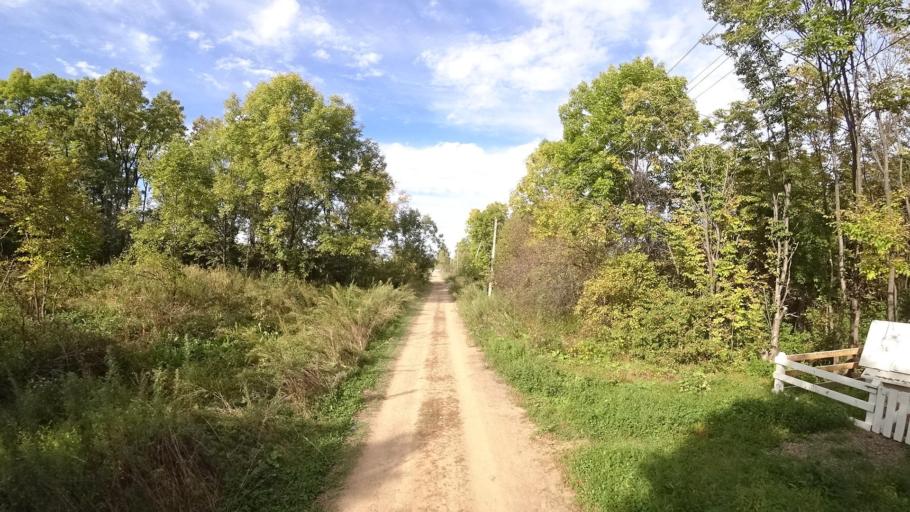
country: RU
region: Primorskiy
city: Dostoyevka
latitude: 44.2940
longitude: 133.4588
